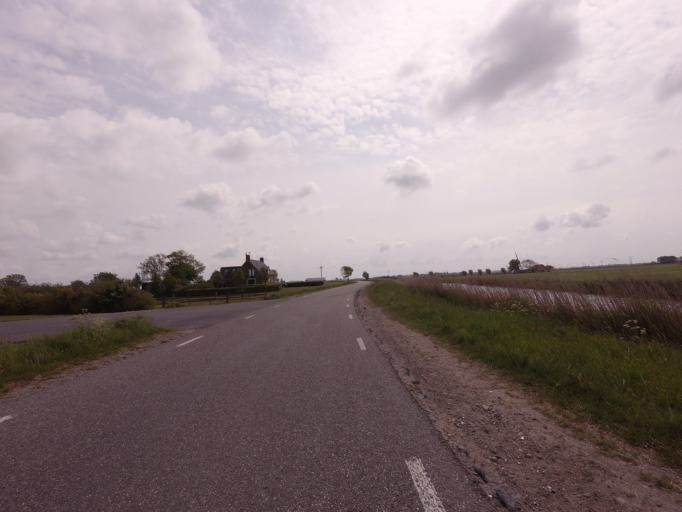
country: NL
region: Friesland
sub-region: Sudwest Fryslan
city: Bolsward
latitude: 53.1043
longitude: 5.5121
